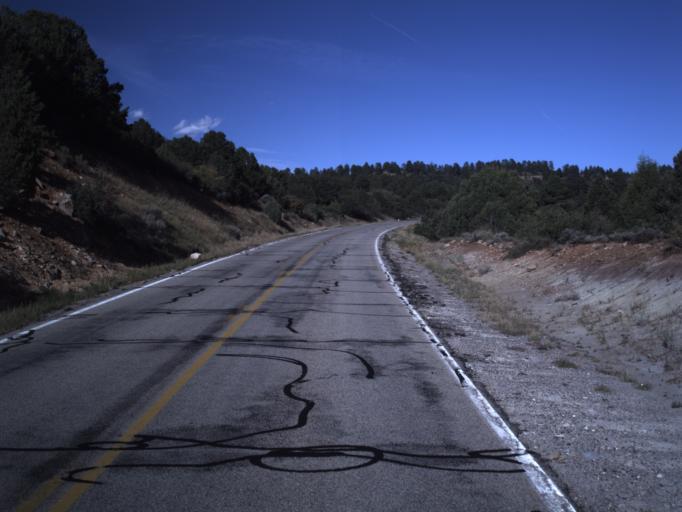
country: US
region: Utah
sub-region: Grand County
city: Moab
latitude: 38.3331
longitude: -109.2178
